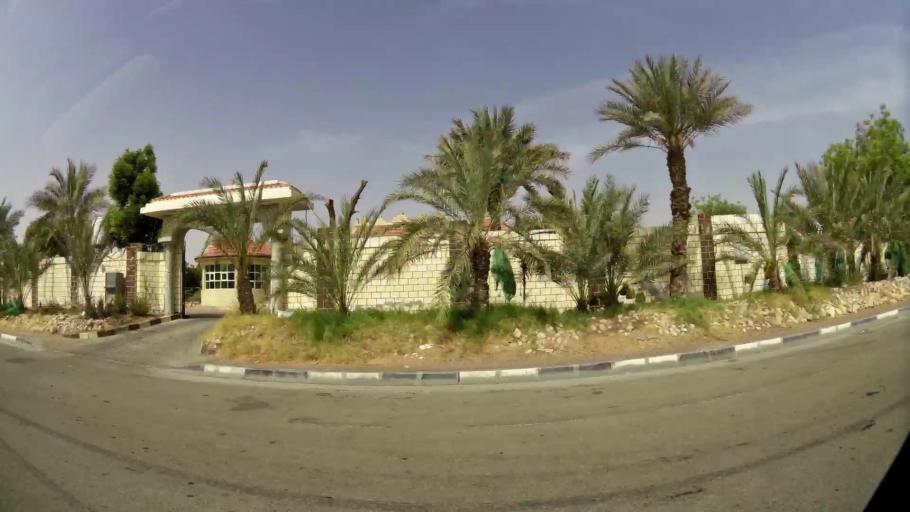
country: AE
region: Abu Dhabi
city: Al Ain
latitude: 24.1618
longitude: 55.6769
